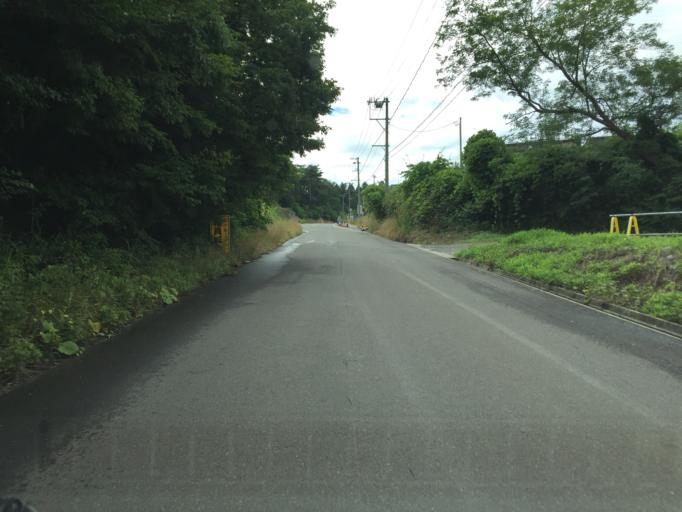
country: JP
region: Miyagi
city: Marumori
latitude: 37.8160
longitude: 140.9511
